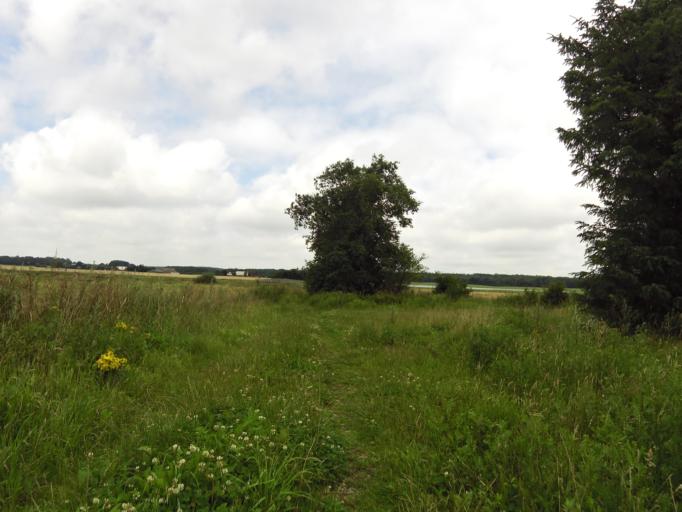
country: DK
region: South Denmark
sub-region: Haderslev Kommune
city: Gram
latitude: 55.2967
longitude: 9.0411
